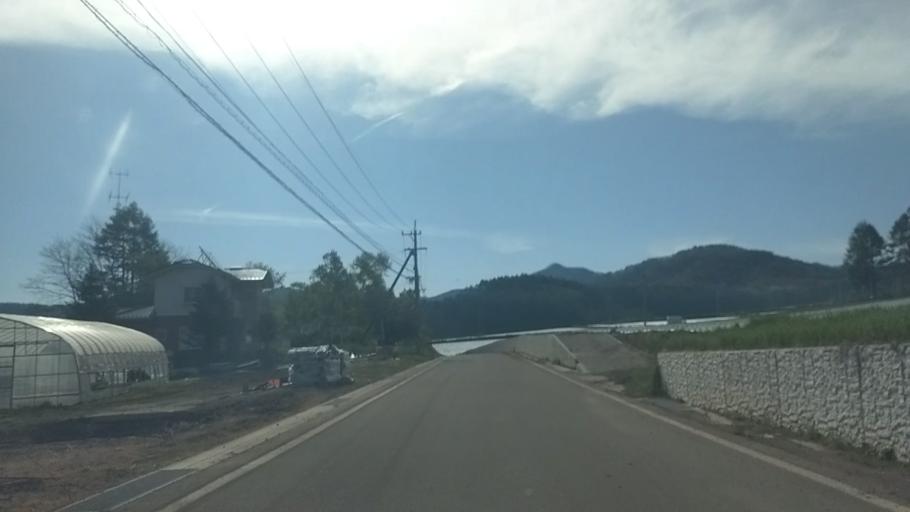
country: JP
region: Yamanashi
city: Nirasaki
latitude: 35.9363
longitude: 138.4714
